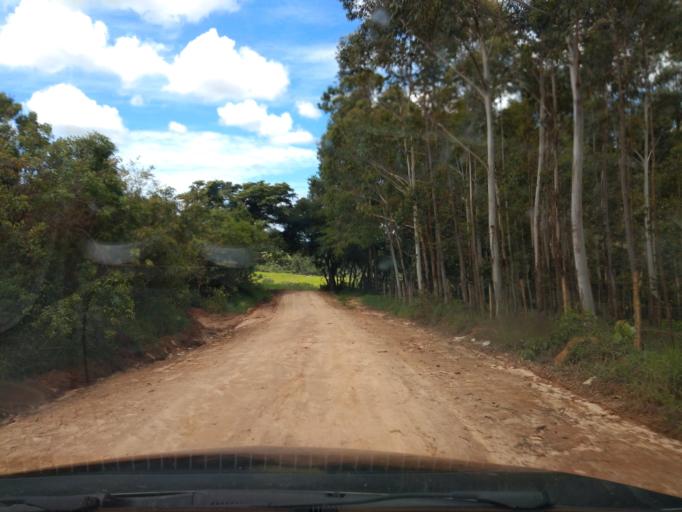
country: BR
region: Minas Gerais
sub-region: Lavras
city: Lavras
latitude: -21.5092
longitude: -44.9254
